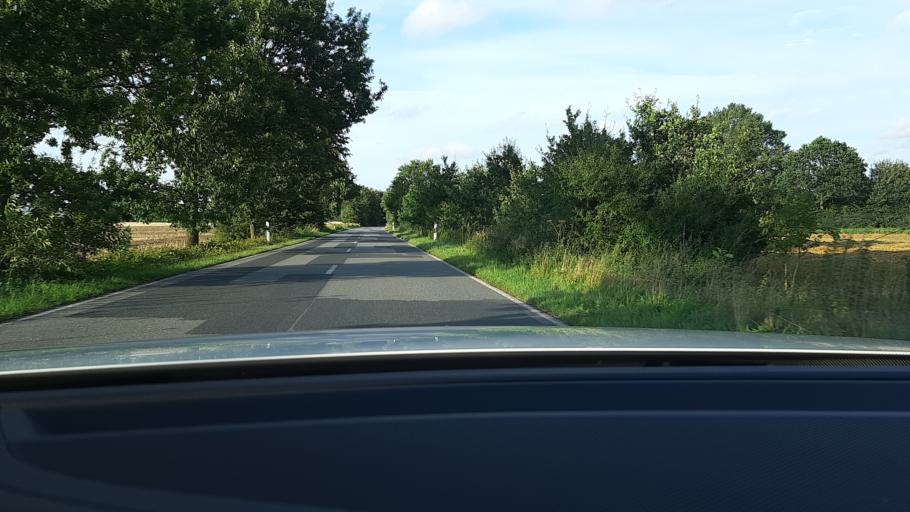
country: DE
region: Schleswig-Holstein
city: Monkhagen
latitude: 53.9300
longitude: 10.5814
